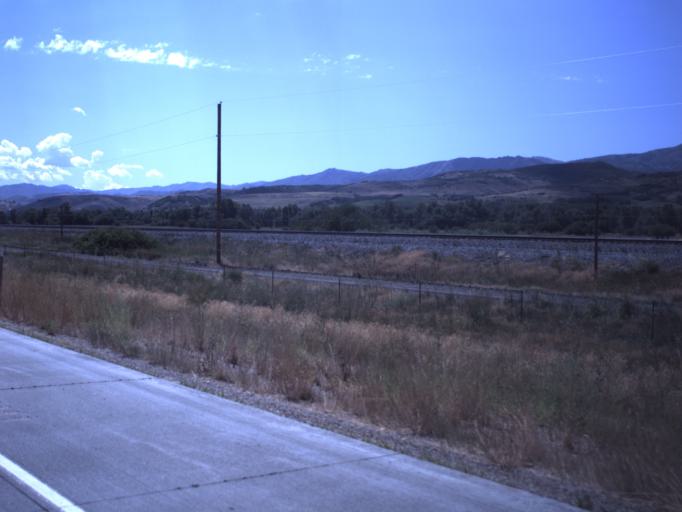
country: US
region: Utah
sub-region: Morgan County
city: Mountain Green
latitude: 41.1058
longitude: -111.7473
